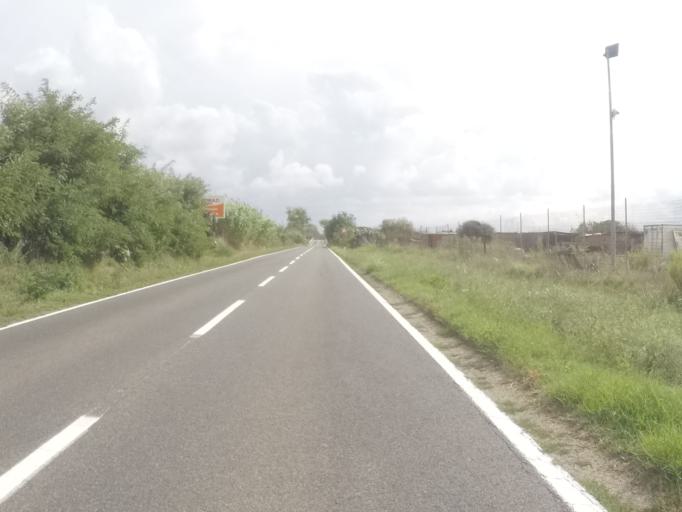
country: IT
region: Sardinia
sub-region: Provincia di Oristano
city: Terralba
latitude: 39.7036
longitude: 8.6394
